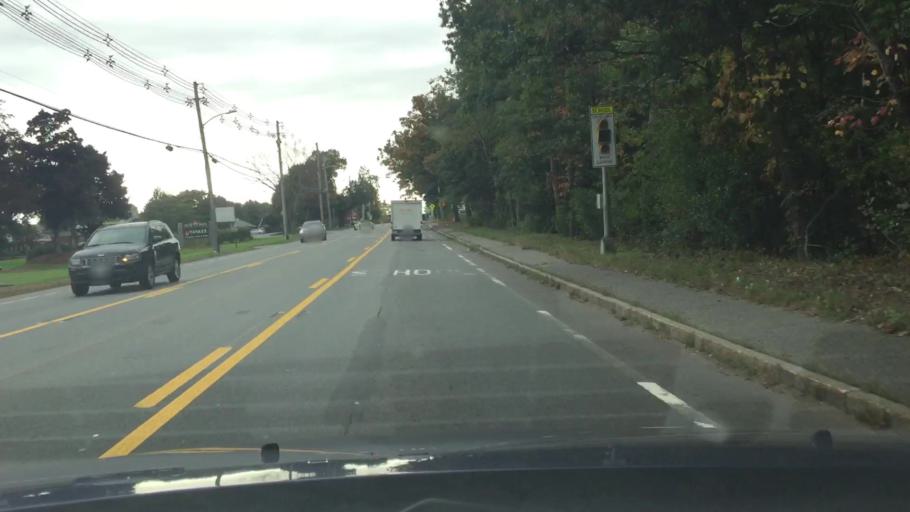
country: US
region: Massachusetts
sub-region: Essex County
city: Middleton
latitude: 42.5856
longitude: -71.0086
